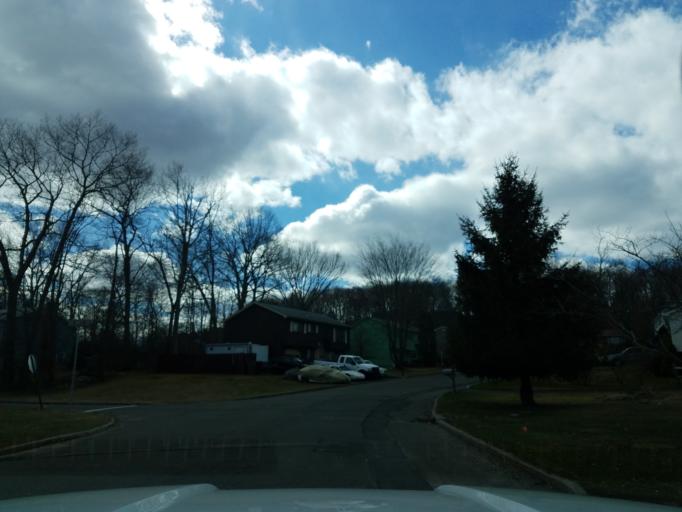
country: US
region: Connecticut
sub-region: New Haven County
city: Prospect
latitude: 41.4792
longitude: -73.0060
